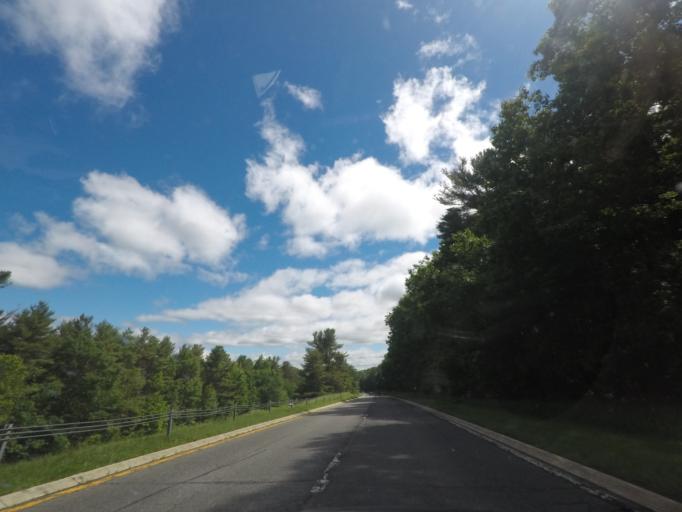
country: US
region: New York
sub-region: Columbia County
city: Chatham
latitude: 42.3028
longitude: -73.5819
